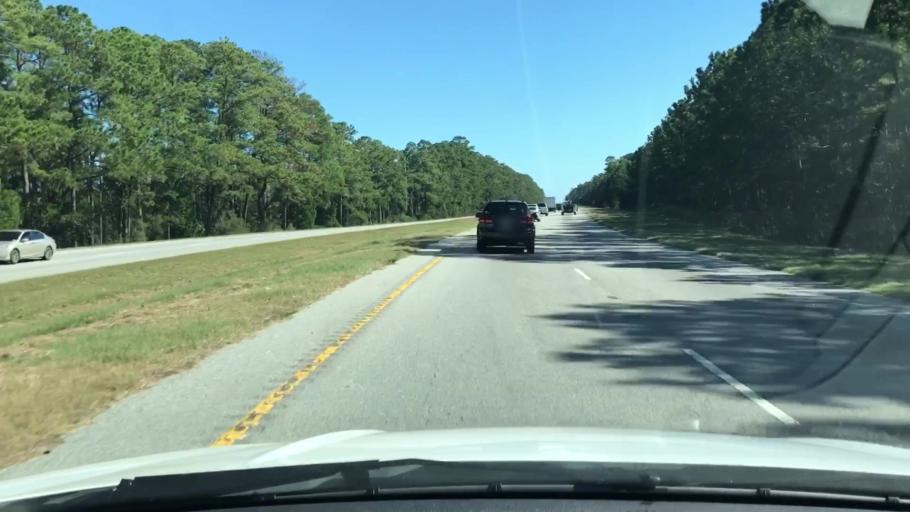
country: US
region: South Carolina
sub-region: Beaufort County
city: Laurel Bay
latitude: 32.3742
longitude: -80.8245
